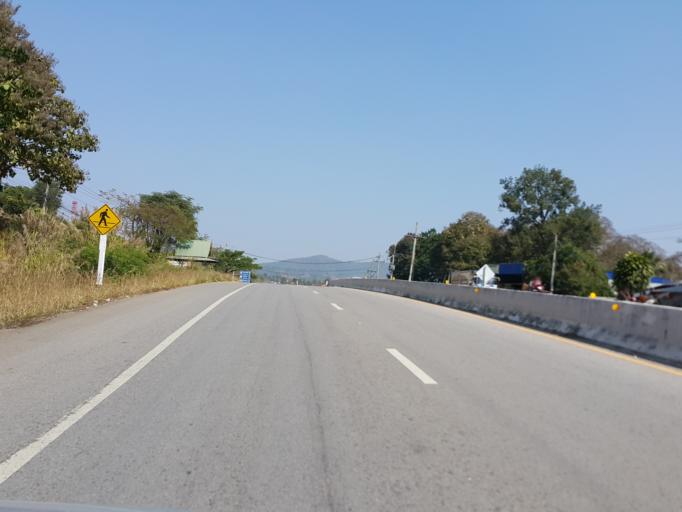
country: TH
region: Lampang
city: Wang Nuea
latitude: 19.1202
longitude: 99.4775
